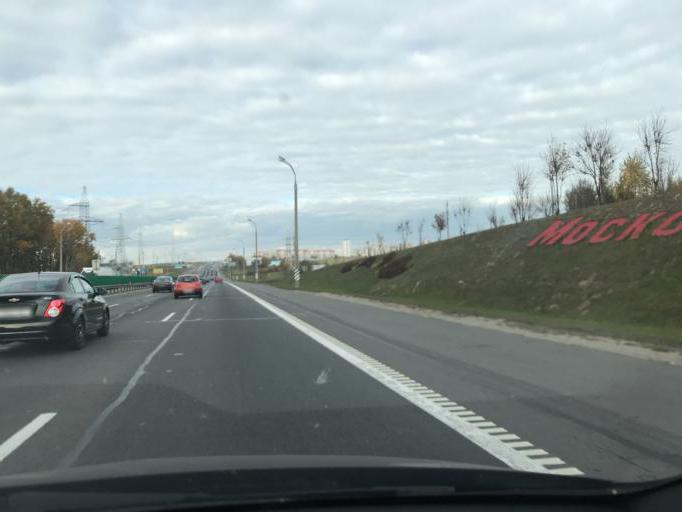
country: BY
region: Minsk
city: Malinovka
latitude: 53.8651
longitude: 27.4253
